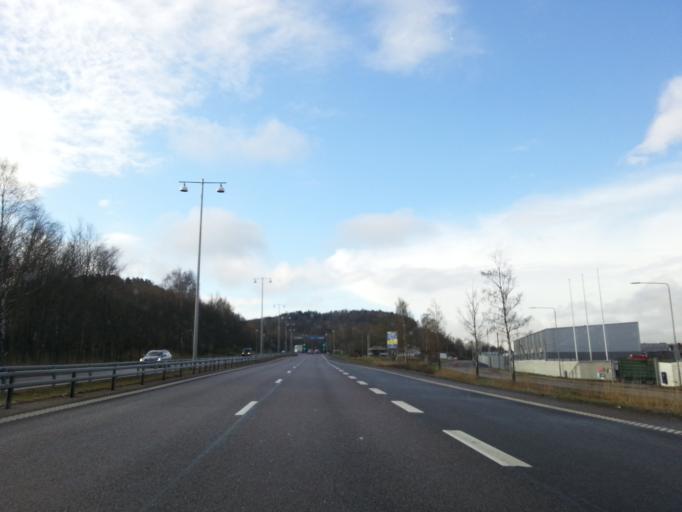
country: SE
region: Vaestra Goetaland
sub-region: Goteborg
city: Gardsten
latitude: 57.7926
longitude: 12.0156
